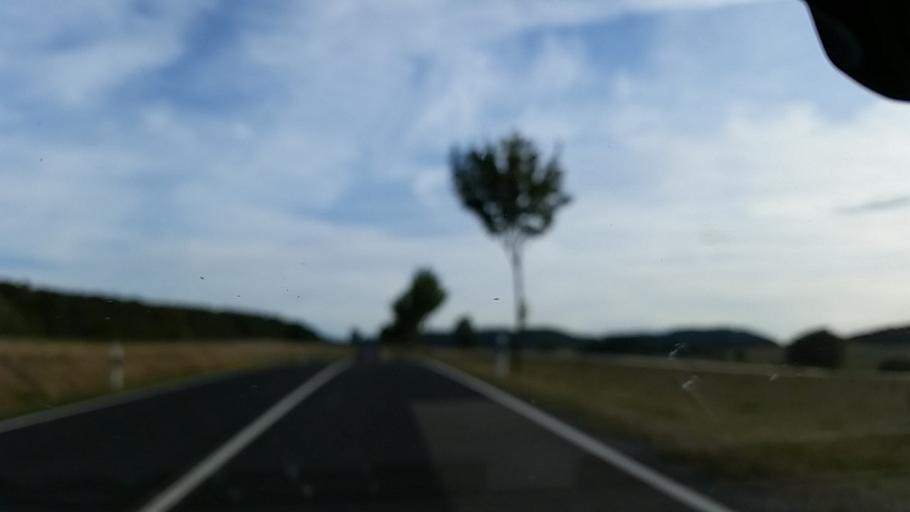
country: DE
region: Thuringia
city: Henneberg
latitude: 50.5106
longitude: 10.3579
